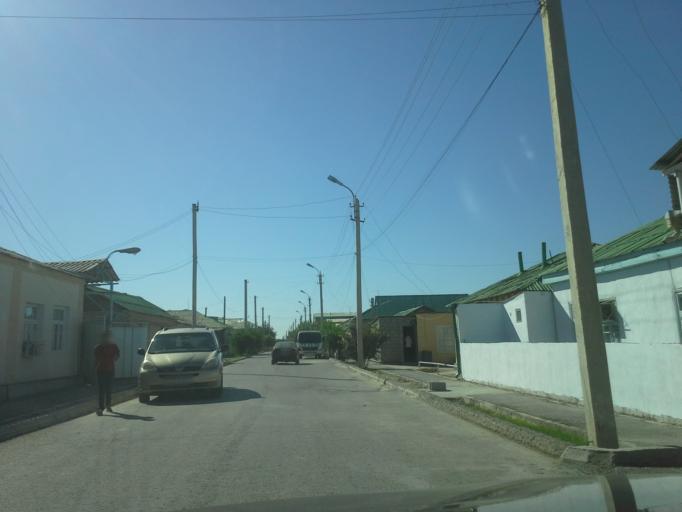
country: TM
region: Ahal
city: Abadan
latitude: 38.0717
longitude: 58.1536
